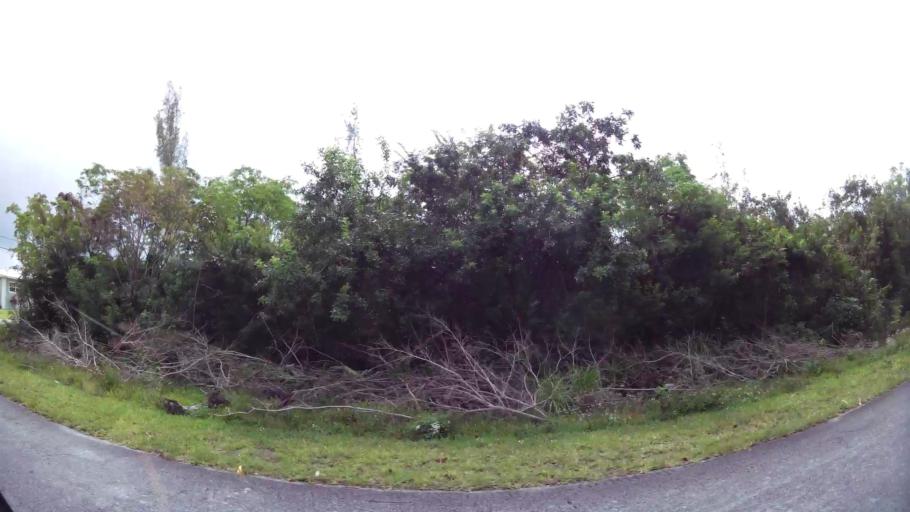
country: BS
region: Freeport
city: Lucaya
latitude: 26.5419
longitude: -78.5968
